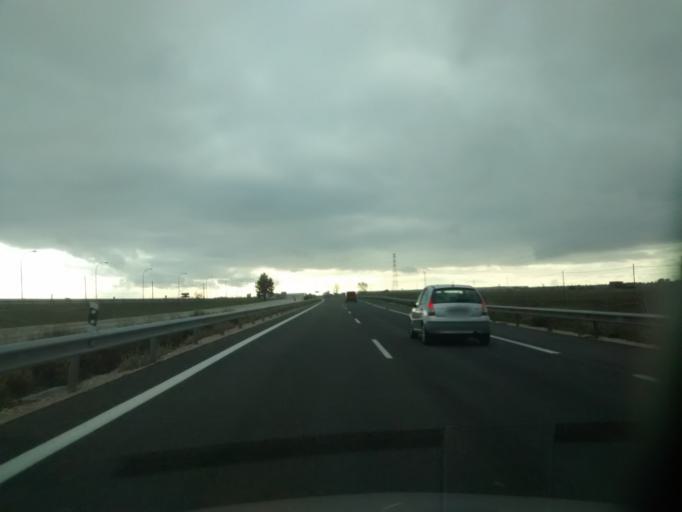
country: ES
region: Castille-La Mancha
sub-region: Provincia de Guadalajara
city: Trijueque
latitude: 40.7616
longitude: -3.0112
